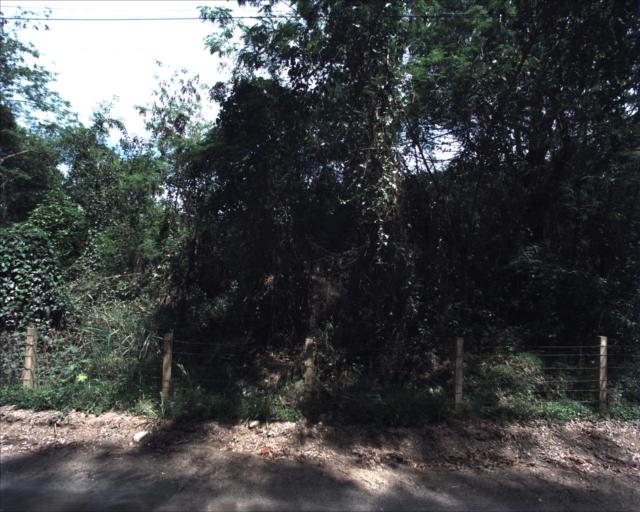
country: BR
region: Sao Paulo
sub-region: Aracoiaba Da Serra
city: Aracoiaba da Serra
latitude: -23.5553
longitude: -47.5372
